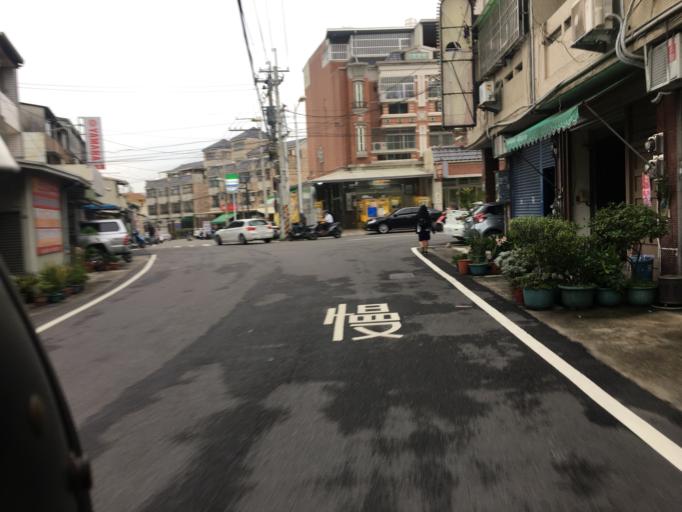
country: TW
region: Taiwan
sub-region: Taichung City
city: Taichung
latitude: 24.0978
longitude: 120.7025
